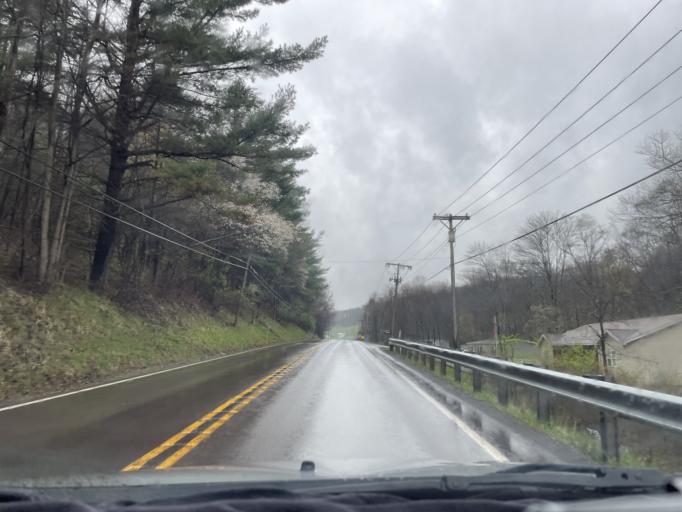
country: US
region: Maryland
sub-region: Garrett County
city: Mountain Lake Park
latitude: 39.4543
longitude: -79.2551
